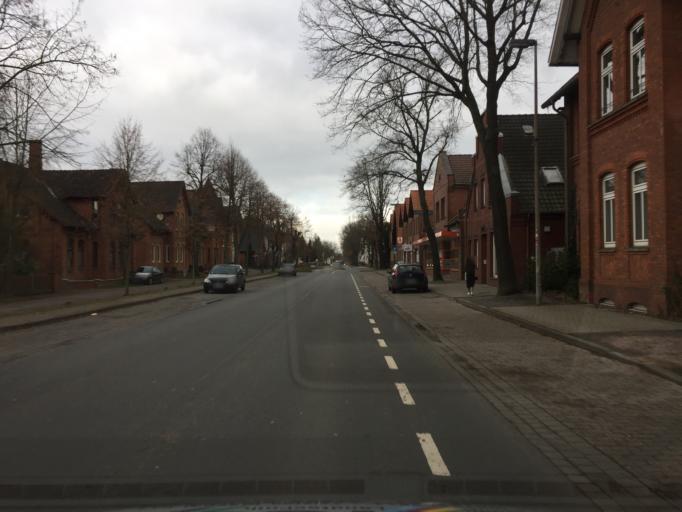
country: DE
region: Lower Saxony
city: Stolzenau
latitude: 52.5128
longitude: 9.0767
